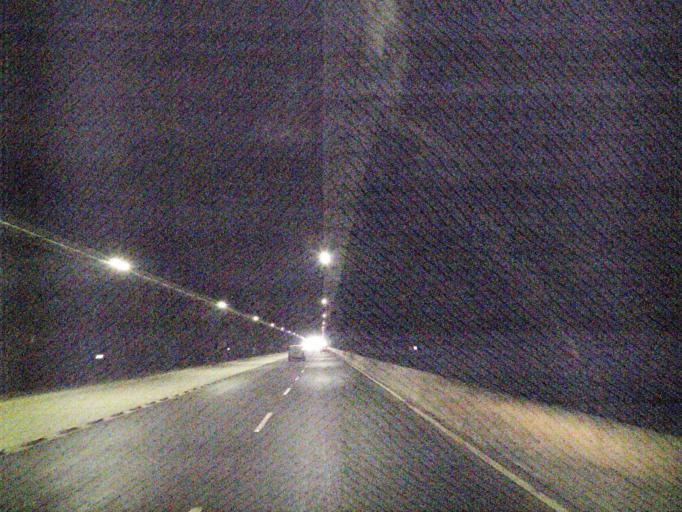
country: BR
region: Rio de Janeiro
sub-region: Niteroi
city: Niteroi
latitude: -22.9335
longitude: -43.0937
